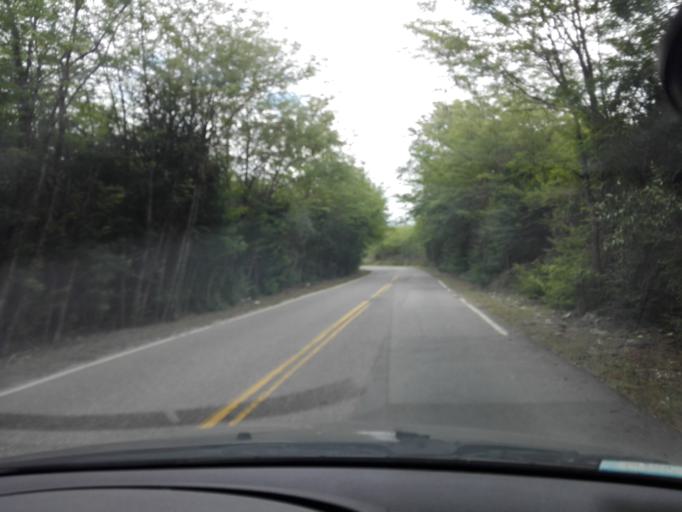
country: AR
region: Cordoba
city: Cuesta Blanca
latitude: -31.5914
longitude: -64.5677
